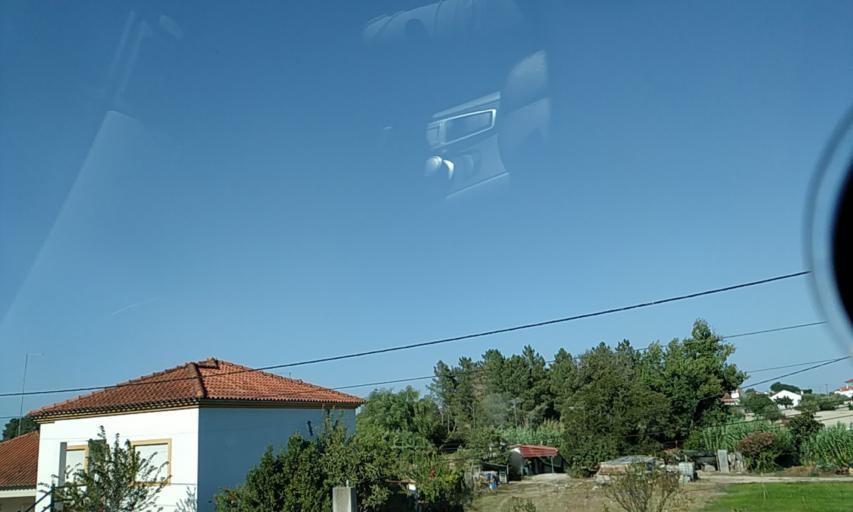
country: PT
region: Santarem
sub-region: Coruche
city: Coruche
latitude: 38.9703
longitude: -8.5368
